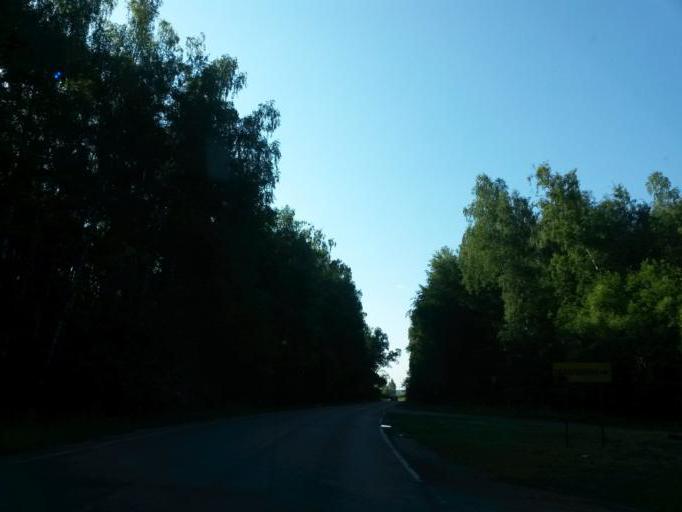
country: RU
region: Moskovskaya
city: Melikhovo
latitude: 55.2152
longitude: 37.6855
